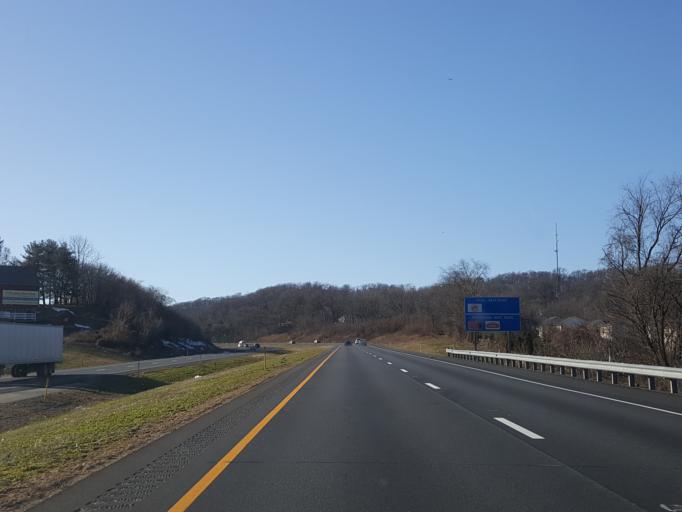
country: US
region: Pennsylvania
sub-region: Lancaster County
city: Columbia
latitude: 40.0428
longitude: -76.4840
